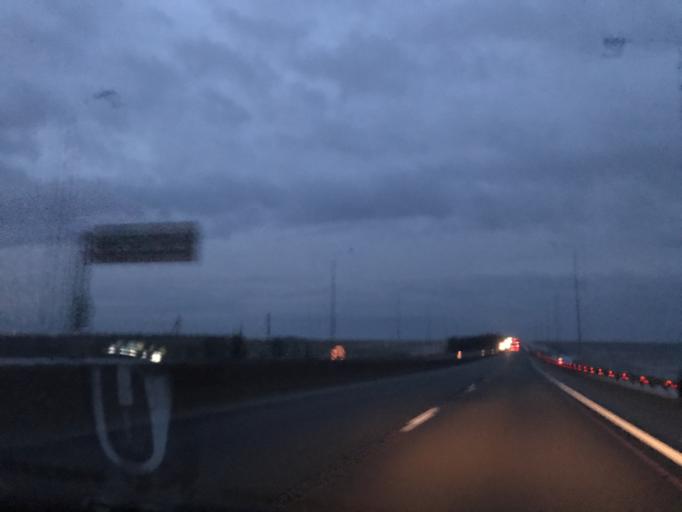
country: RU
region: Rostov
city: Samarskoye
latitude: 46.9994
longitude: 39.7296
